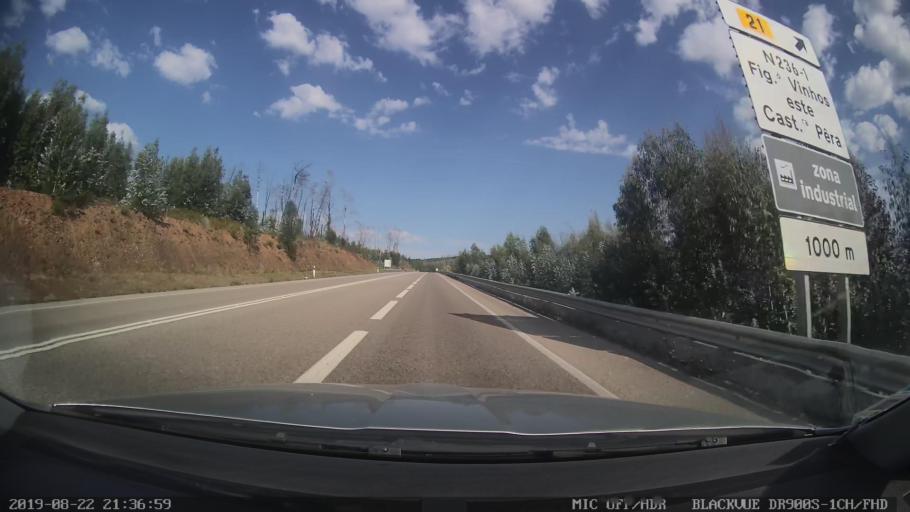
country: PT
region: Leiria
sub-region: Figueiro Dos Vinhos
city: Figueiro dos Vinhos
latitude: 39.9279
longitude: -8.2393
